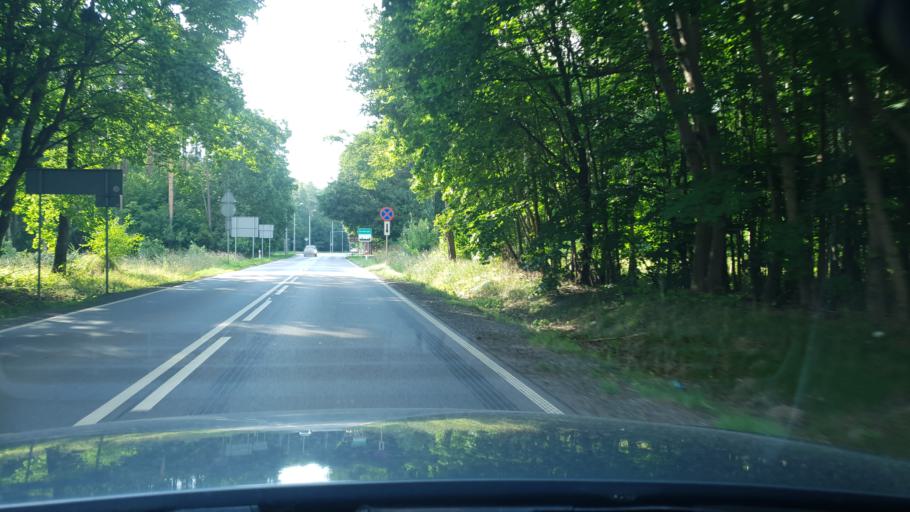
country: PL
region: Kujawsko-Pomorskie
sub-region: Grudziadz
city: Grudziadz
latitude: 53.4454
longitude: 18.8150
